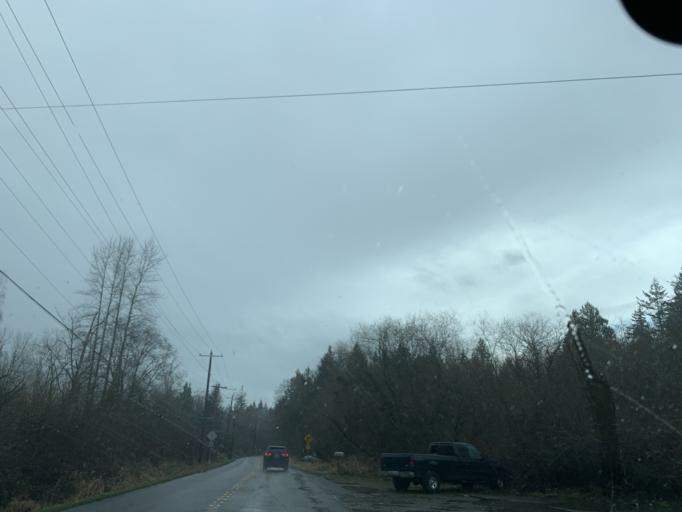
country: US
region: Washington
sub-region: Snohomish County
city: Alderwood Manor
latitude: 47.8443
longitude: -122.2678
